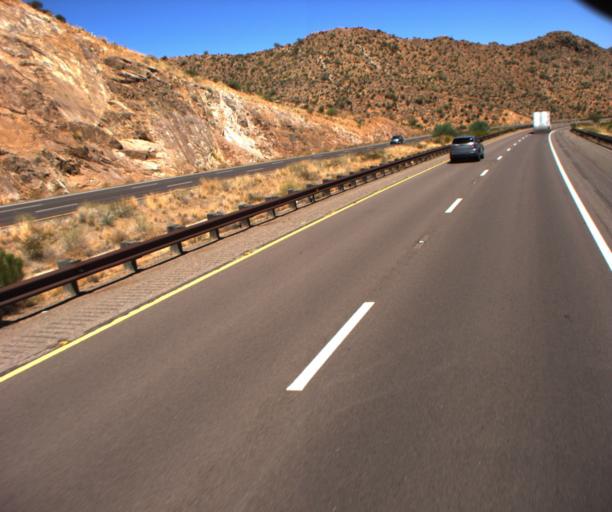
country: US
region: Arizona
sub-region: Maricopa County
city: Rio Verde
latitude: 33.7037
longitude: -111.5049
